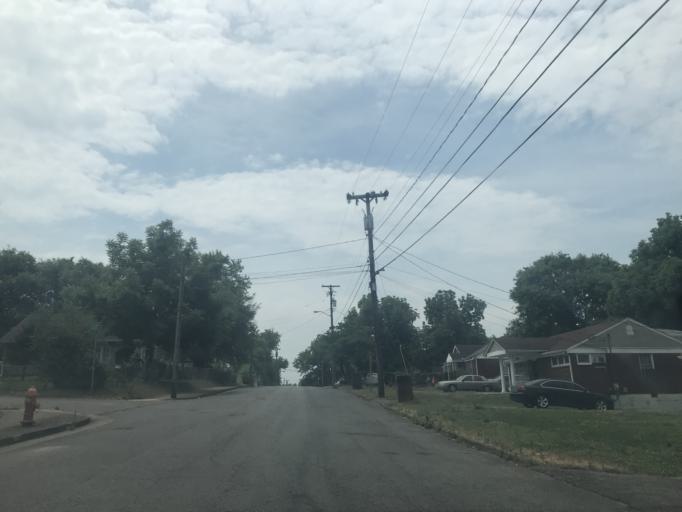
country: US
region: Tennessee
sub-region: Davidson County
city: Nashville
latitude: 36.1839
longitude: -86.8174
